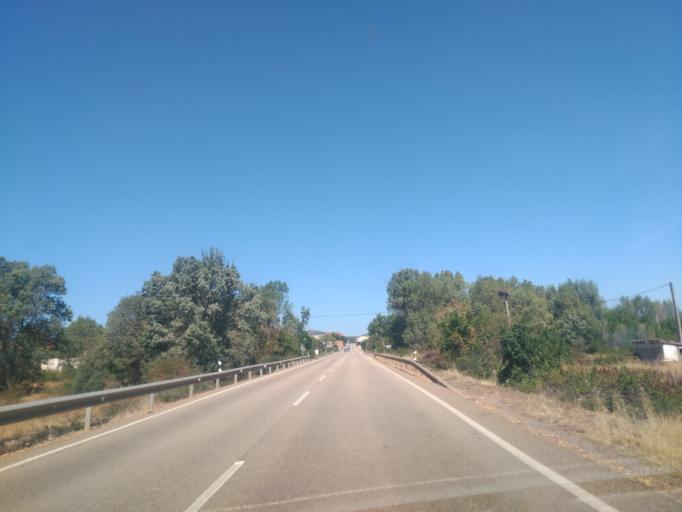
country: ES
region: Castille and Leon
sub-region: Provincia de Zamora
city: Tabara
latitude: 41.8230
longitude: -5.9532
